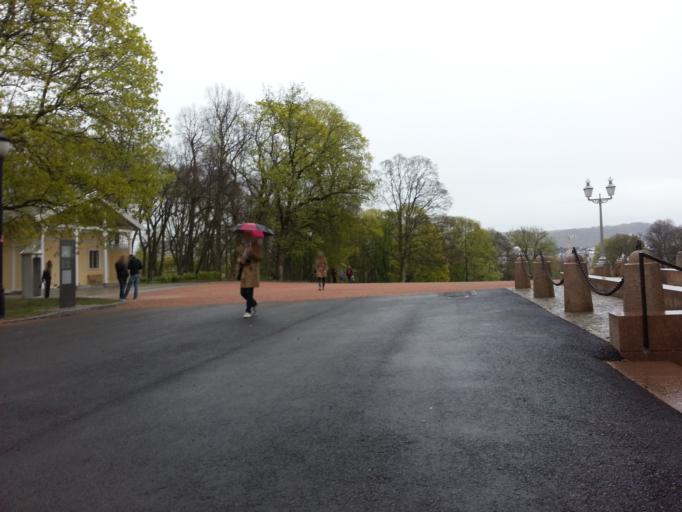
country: NO
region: Oslo
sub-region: Oslo
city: Oslo
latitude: 59.9175
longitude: 10.7280
